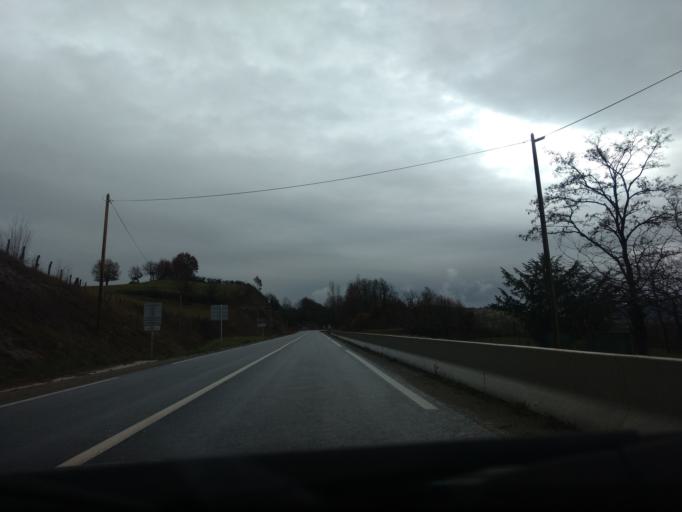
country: FR
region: Midi-Pyrenees
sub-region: Departement de l'Aveyron
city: Firmi
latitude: 44.5121
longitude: 2.3596
